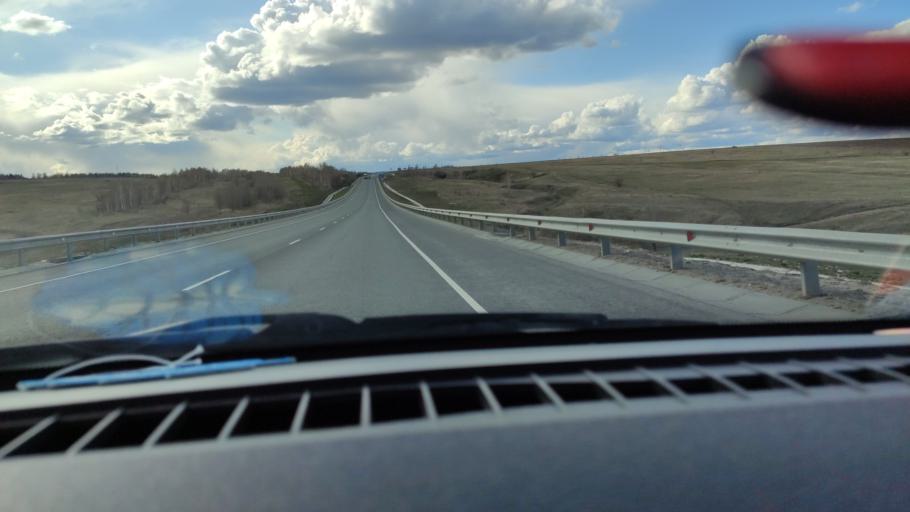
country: RU
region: Saratov
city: Shikhany
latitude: 52.1274
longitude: 47.2371
